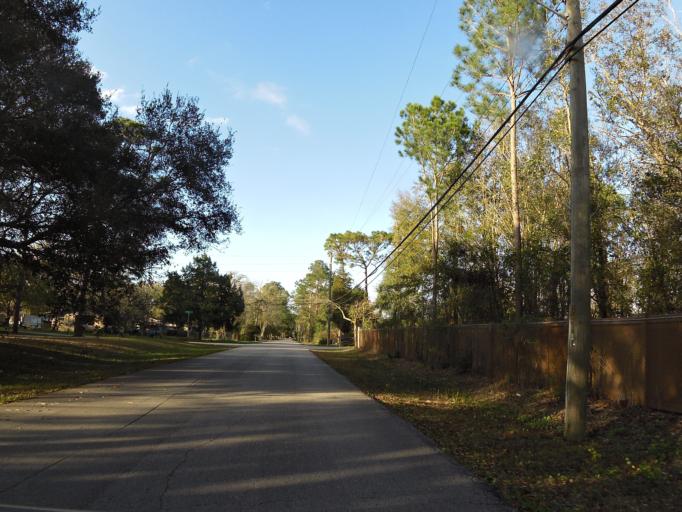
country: US
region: Florida
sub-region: Duval County
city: Jacksonville
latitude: 30.2675
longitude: -81.5741
